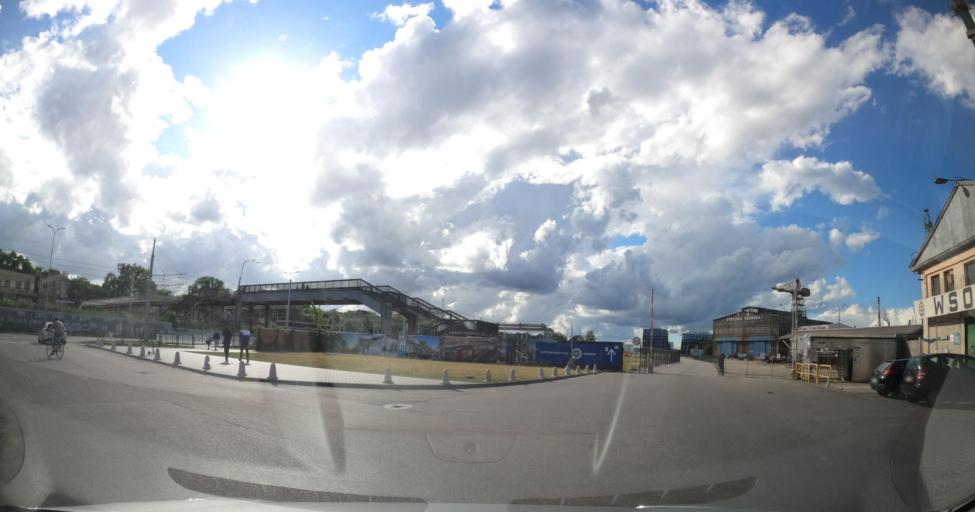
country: PL
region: Pomeranian Voivodeship
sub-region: Gdansk
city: Gdansk
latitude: 54.3645
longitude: 18.6432
